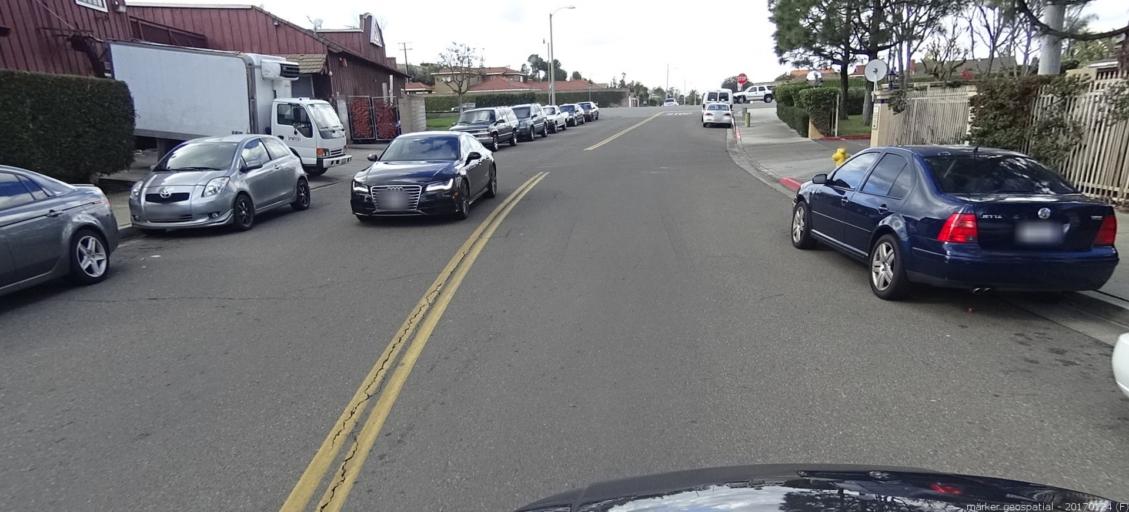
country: US
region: California
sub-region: Orange County
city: Laguna Hills
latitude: 33.6213
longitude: -117.6981
